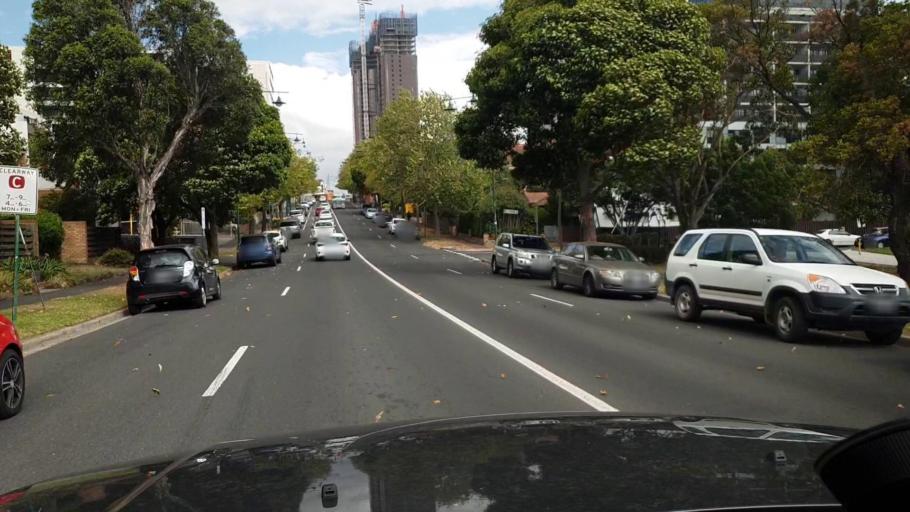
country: AU
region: Victoria
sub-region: Whitehorse
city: Box Hill
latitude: -37.8158
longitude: 145.1244
